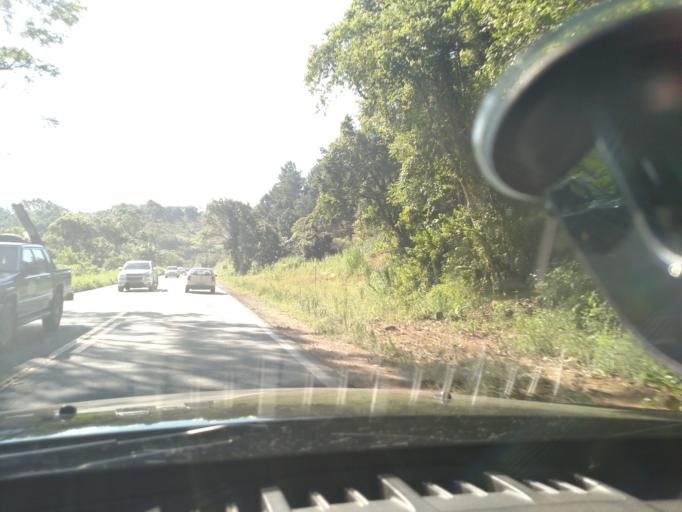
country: BR
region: Santa Catarina
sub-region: Ibirama
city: Ibirama
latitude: -27.0824
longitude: -49.5116
